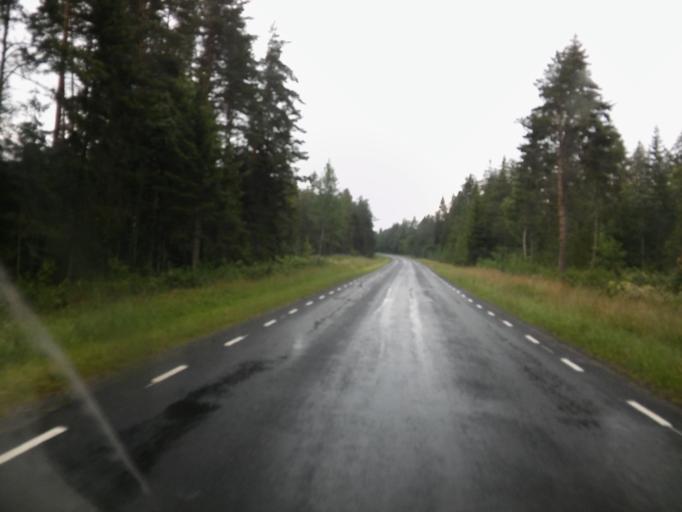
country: EE
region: Raplamaa
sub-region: Rapla vald
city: Rapla
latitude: 58.8814
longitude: 24.7225
